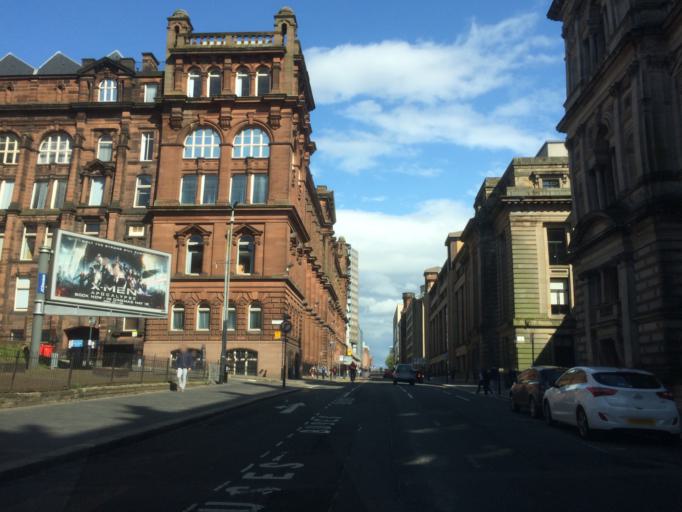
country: GB
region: Scotland
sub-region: Glasgow City
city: Glasgow
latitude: 55.8613
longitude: -4.2482
